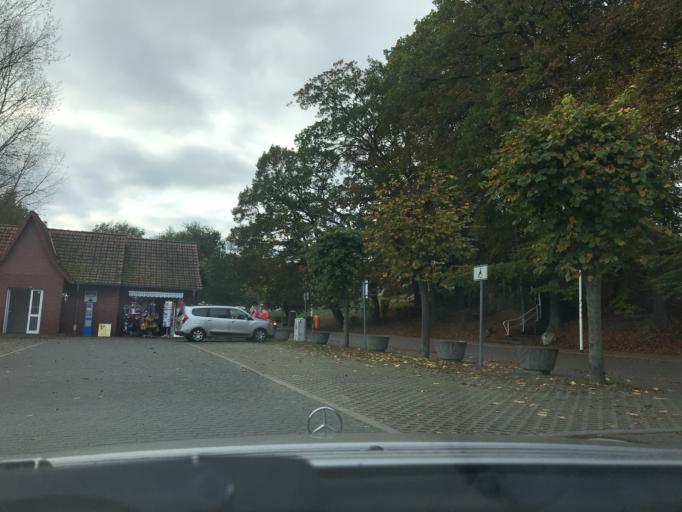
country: DE
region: Mecklenburg-Vorpommern
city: Loddin
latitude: 54.0401
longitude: 14.0277
